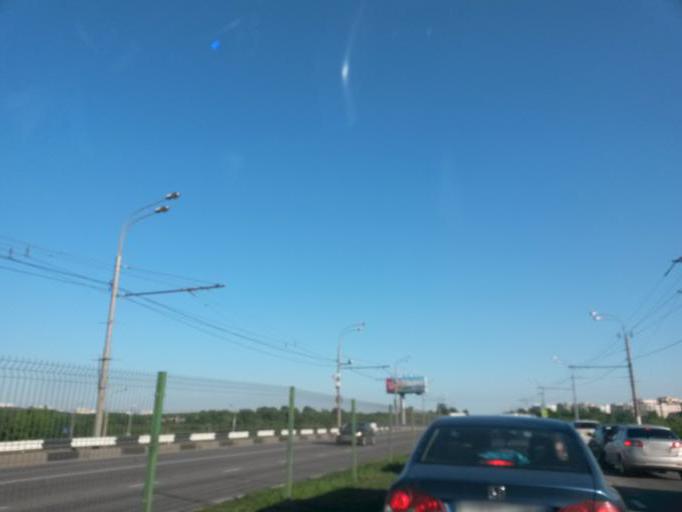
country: RU
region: Moscow
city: Tsaritsyno
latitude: 55.6164
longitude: 37.6585
